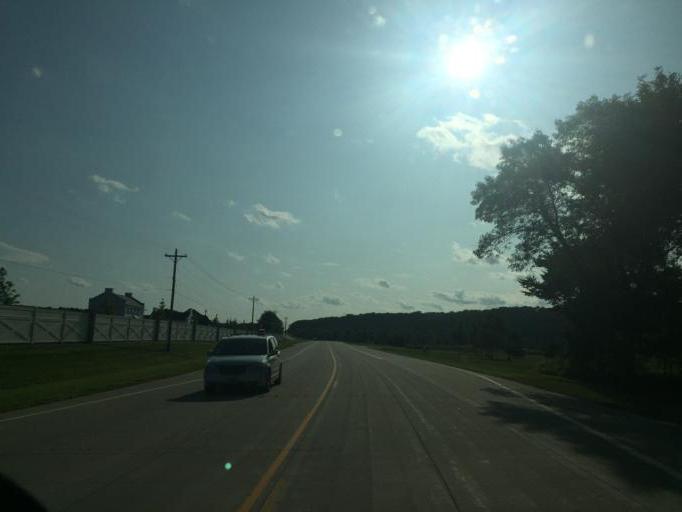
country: US
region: Minnesota
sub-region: Olmsted County
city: Rochester
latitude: 44.0038
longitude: -92.5154
